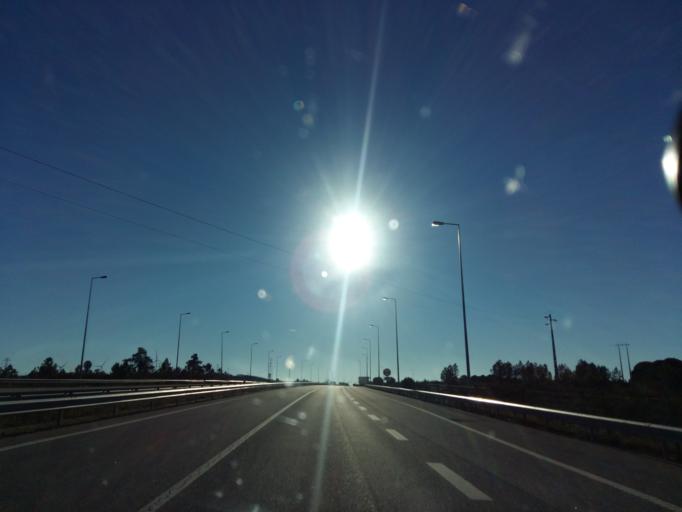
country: PT
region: Castelo Branco
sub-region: Castelo Branco
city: Castelo Branco
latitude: 39.7889
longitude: -7.5666
